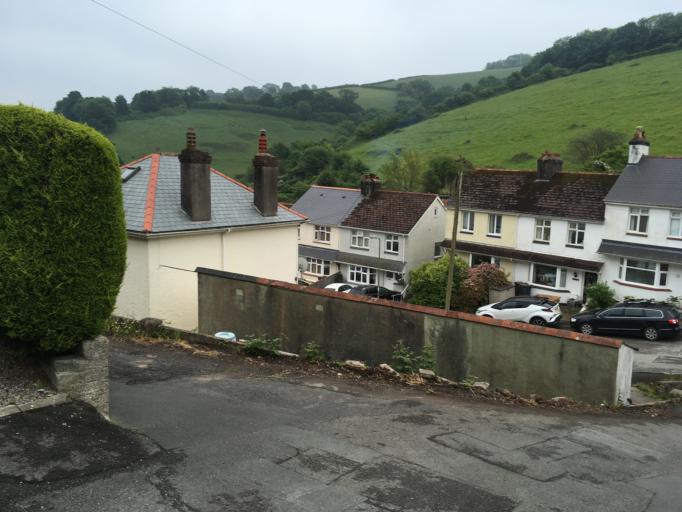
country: GB
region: England
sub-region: Devon
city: Dartmouth
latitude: 50.3491
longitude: -3.5924
